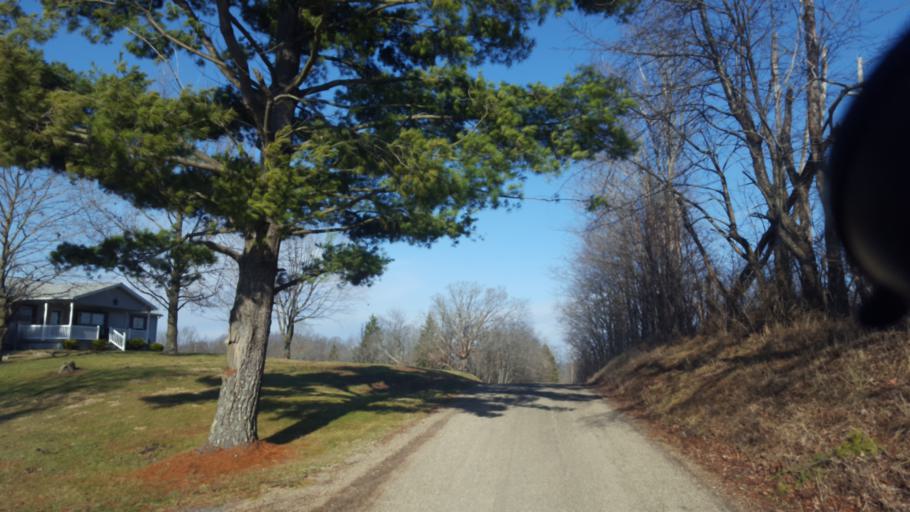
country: US
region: Ohio
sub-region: Guernsey County
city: Cambridge
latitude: 40.0956
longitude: -81.5515
